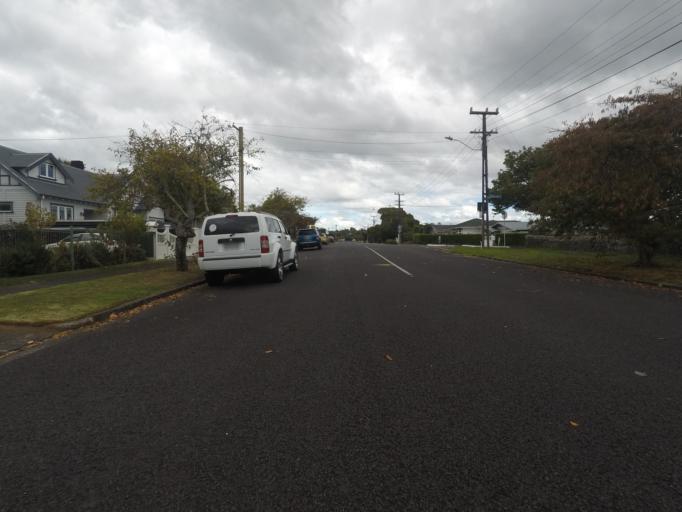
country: NZ
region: Auckland
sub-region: Auckland
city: Auckland
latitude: -36.8752
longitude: 174.7204
